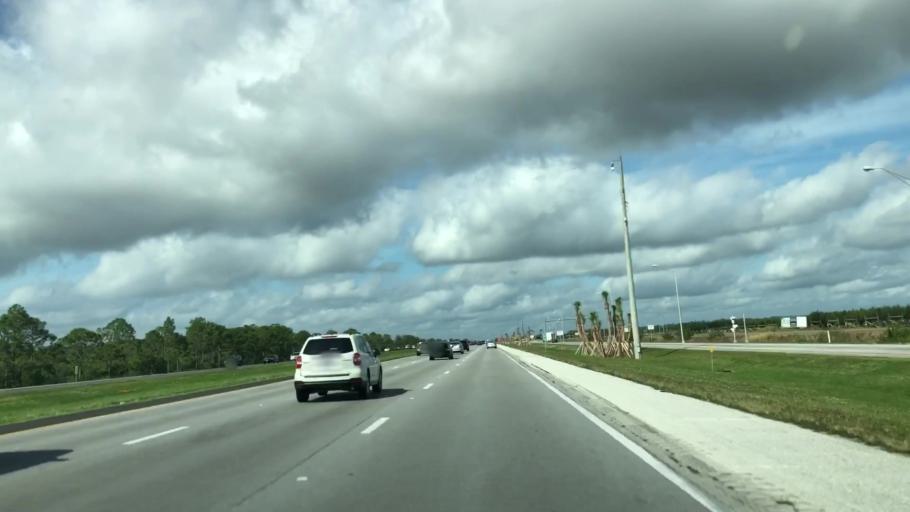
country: US
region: Florida
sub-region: Palm Beach County
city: Tequesta
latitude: 26.9991
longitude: -80.1993
